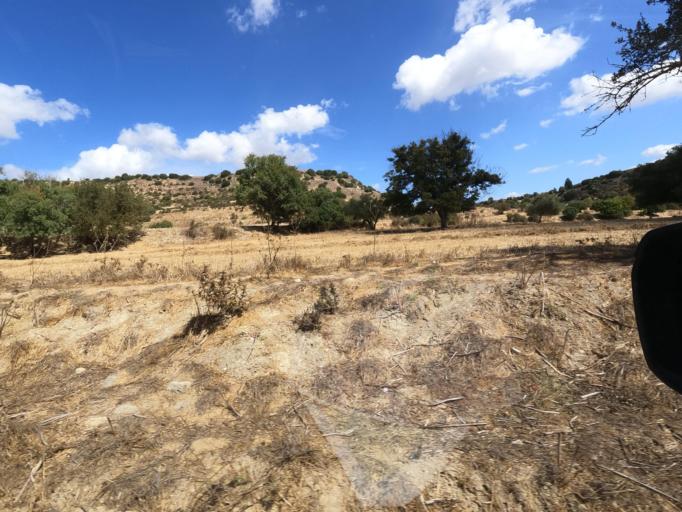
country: CY
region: Pafos
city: Mesogi
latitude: 34.8267
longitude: 32.5496
